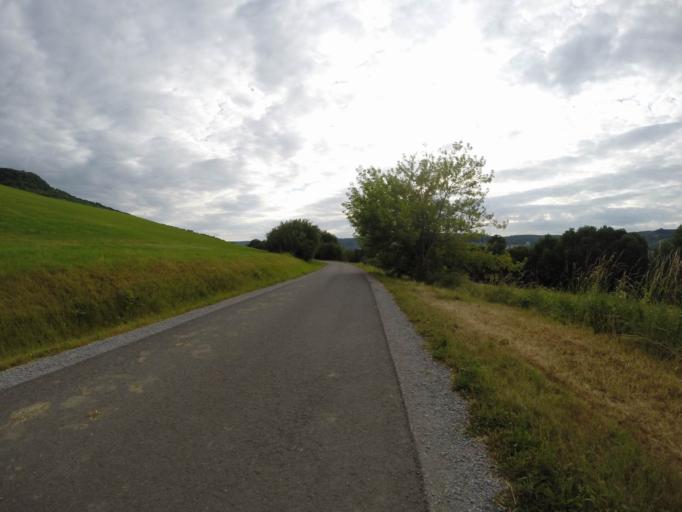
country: DE
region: Thuringia
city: Neuengonna
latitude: 50.9487
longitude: 11.6306
